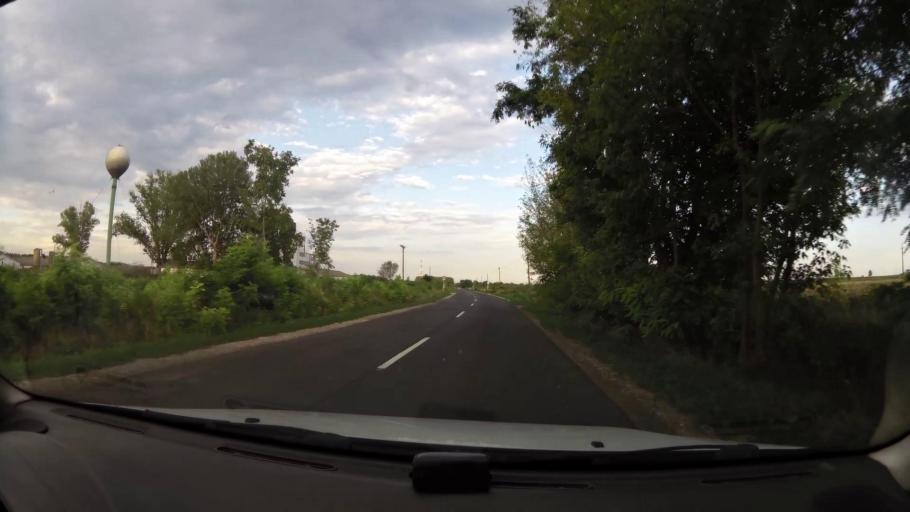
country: HU
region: Pest
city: Tapiobicske
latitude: 47.3490
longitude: 19.7139
